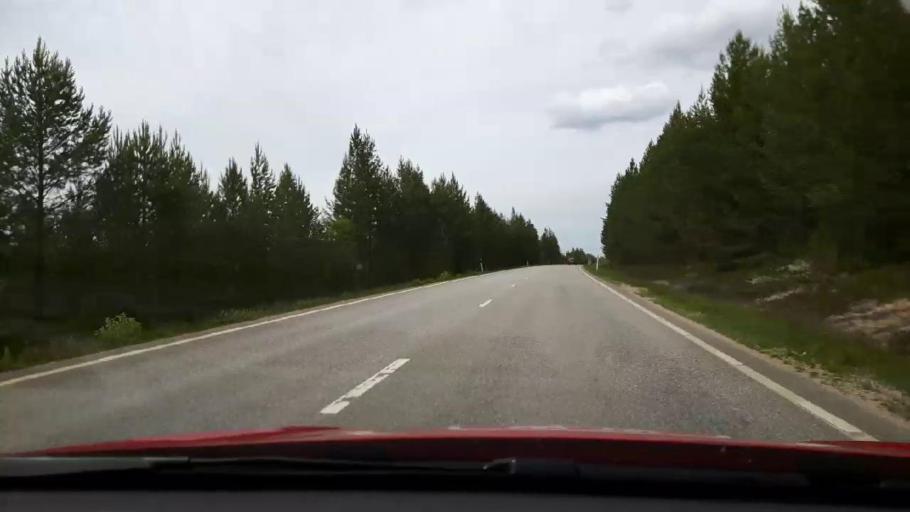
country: SE
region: Jaemtland
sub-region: Harjedalens Kommun
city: Sveg
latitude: 62.0515
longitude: 14.3116
